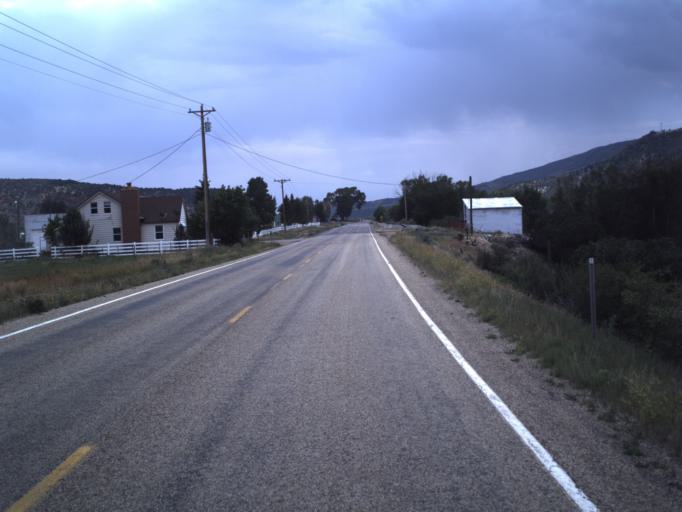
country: US
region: Utah
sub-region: Duchesne County
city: Duchesne
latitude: 40.4333
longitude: -110.8061
